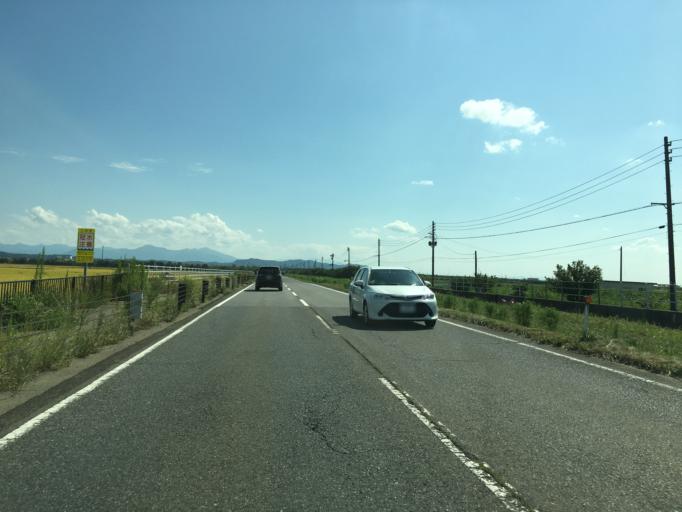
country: JP
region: Niigata
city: Niitsu-honcho
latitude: 37.8289
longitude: 139.0975
